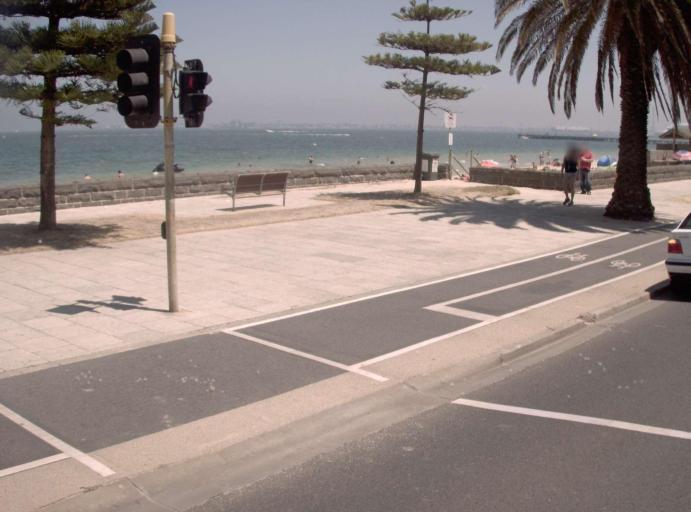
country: AU
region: Victoria
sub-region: Port Phillip
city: Middle Park
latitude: -37.8513
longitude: 144.9557
